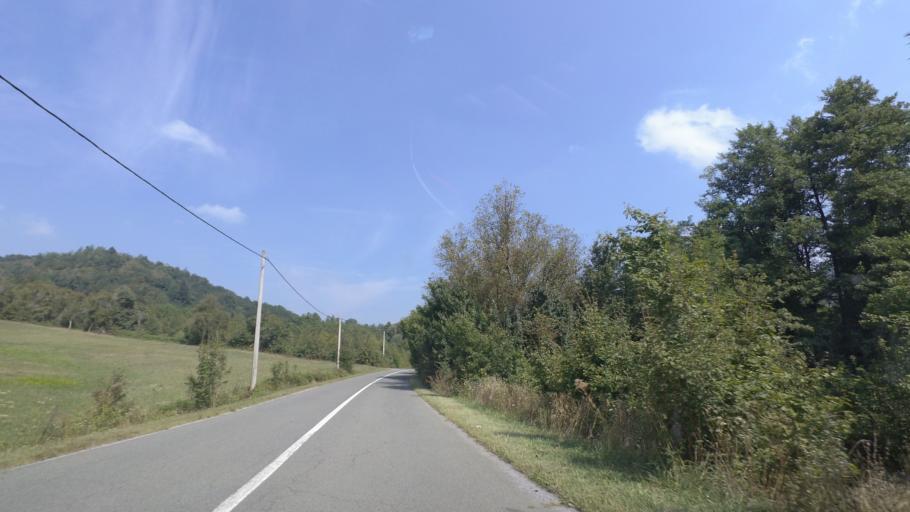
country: BA
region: Federation of Bosnia and Herzegovina
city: Zboriste
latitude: 45.1901
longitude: 16.1258
